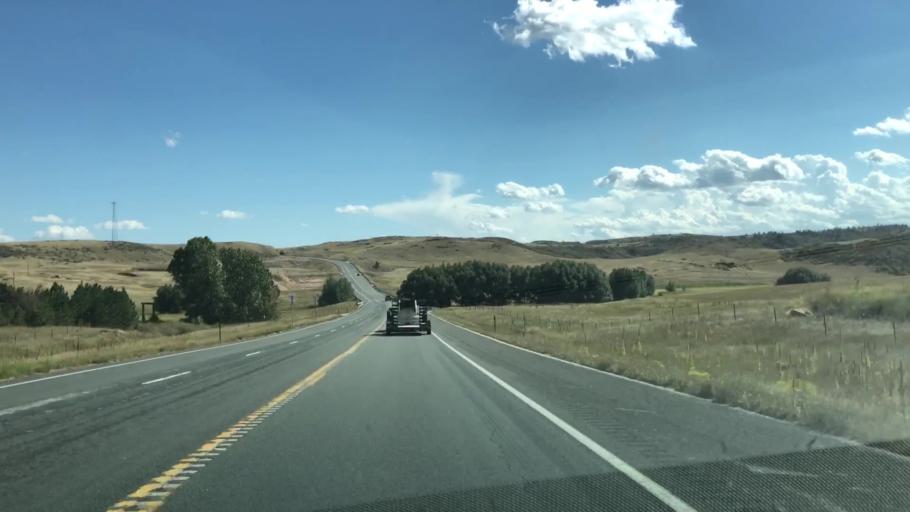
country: US
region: Colorado
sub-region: Larimer County
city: Laporte
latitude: 40.9392
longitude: -105.3427
